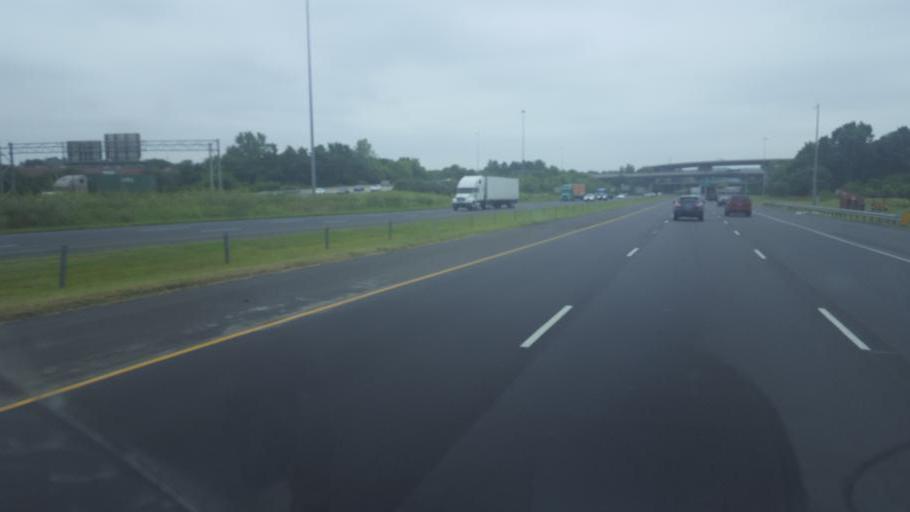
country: US
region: North Carolina
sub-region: Mecklenburg County
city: Pineville
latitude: 35.1207
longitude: -80.9202
